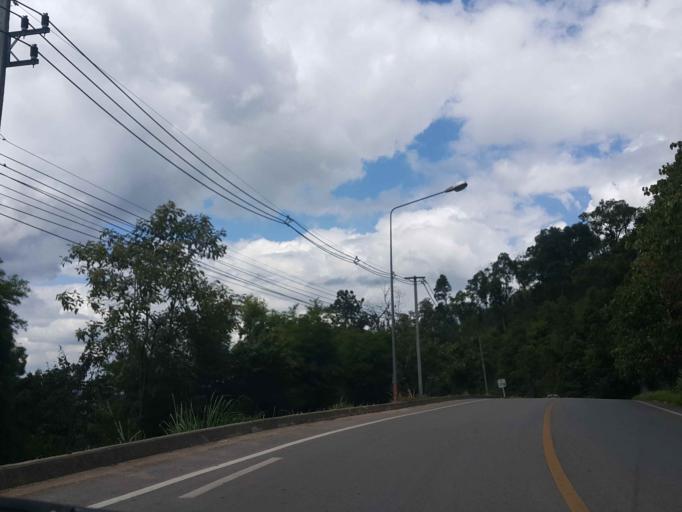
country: TH
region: Chiang Mai
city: Samoeng
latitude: 18.8775
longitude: 98.8025
